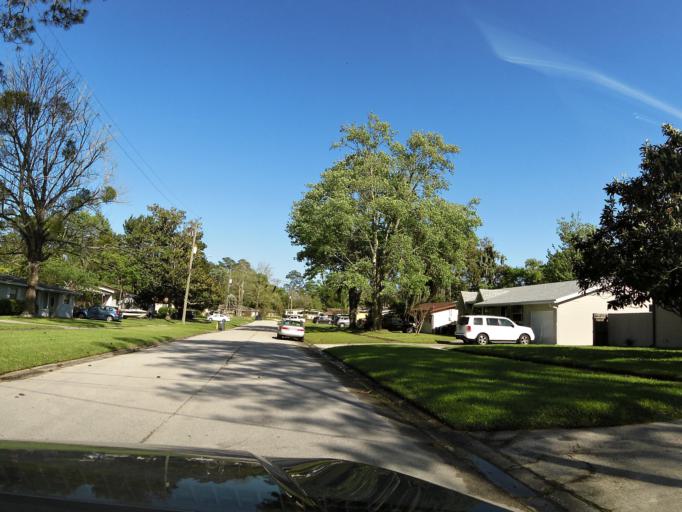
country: US
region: Florida
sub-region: Duval County
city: Jacksonville
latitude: 30.2817
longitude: -81.5990
